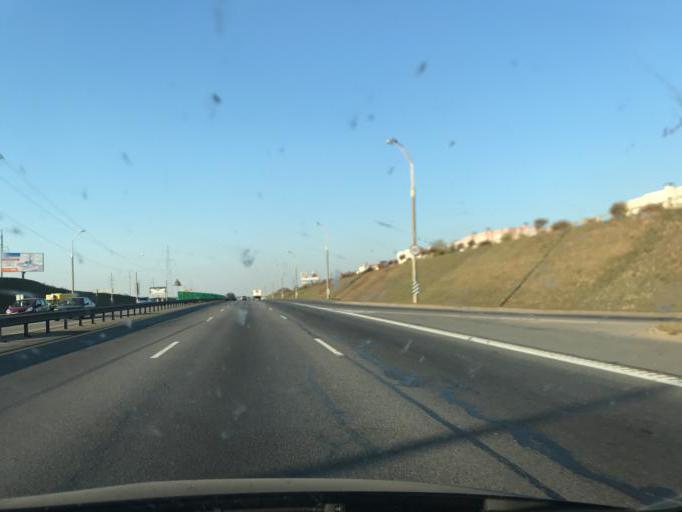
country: BY
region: Minsk
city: Malinovka
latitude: 53.8801
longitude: 27.4174
